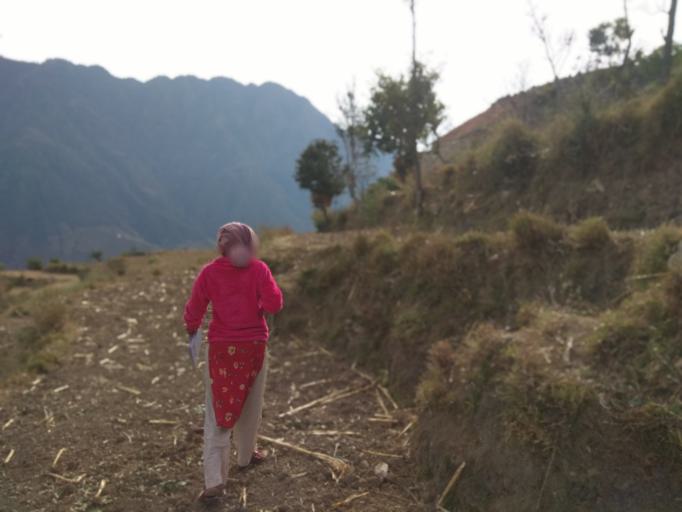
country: NP
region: Mid Western
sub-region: Bheri Zone
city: Dailekh
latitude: 29.2495
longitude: 81.6710
